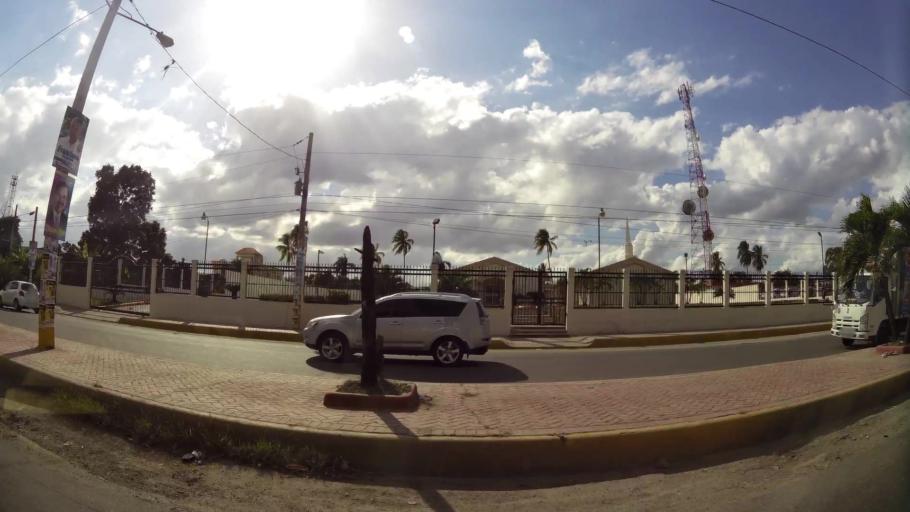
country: DO
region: Nacional
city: Ensanche Luperon
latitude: 18.5505
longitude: -69.9012
